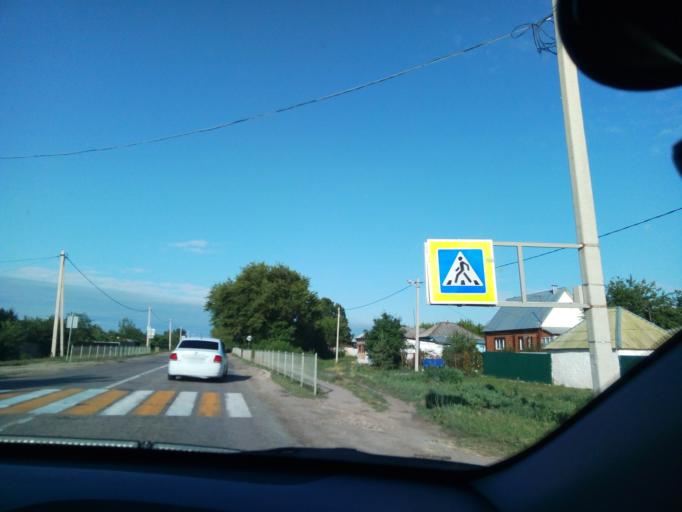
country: RU
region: Rjazan
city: Sasovo
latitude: 54.4163
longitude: 41.9629
